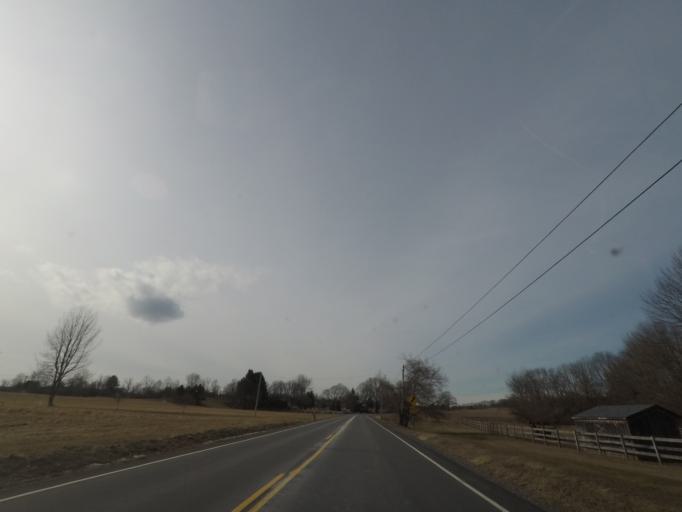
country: US
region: New York
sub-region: Columbia County
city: Valatie
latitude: 42.3962
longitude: -73.6492
